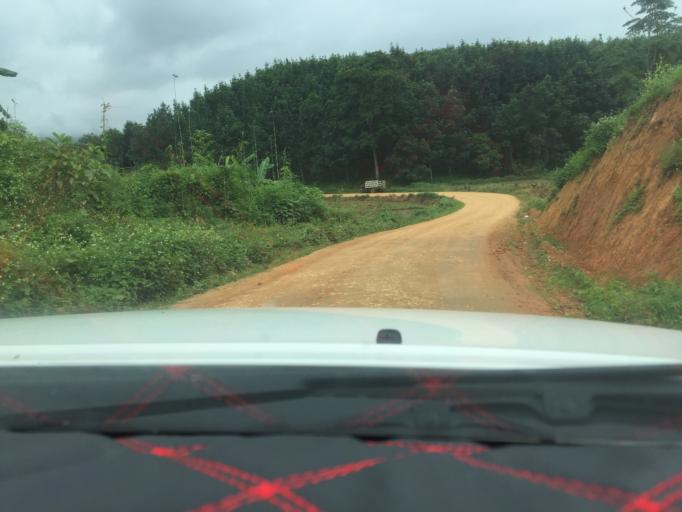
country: TH
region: Phayao
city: Phu Sang
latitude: 19.6946
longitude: 100.5007
